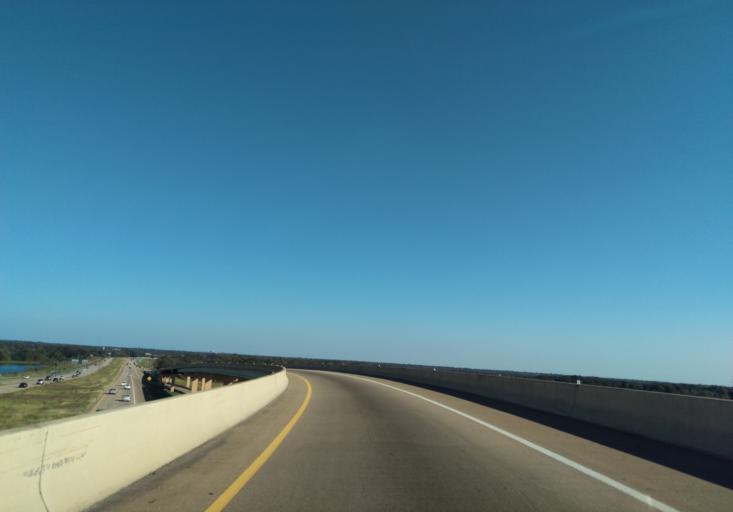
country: US
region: Texas
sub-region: Waller County
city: Hempstead
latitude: 30.1141
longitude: -96.0748
